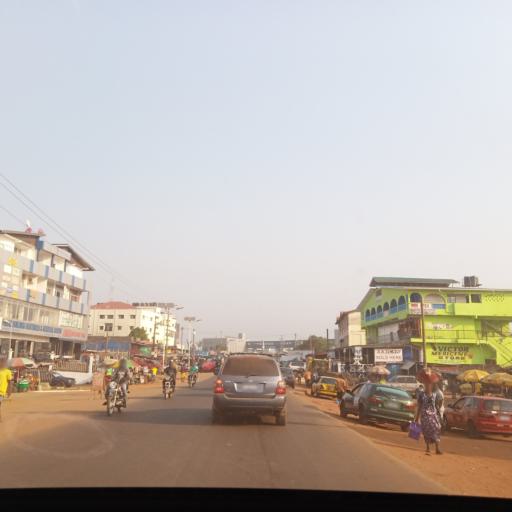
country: LR
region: Montserrado
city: Monrovia
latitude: 6.2624
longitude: -10.7040
